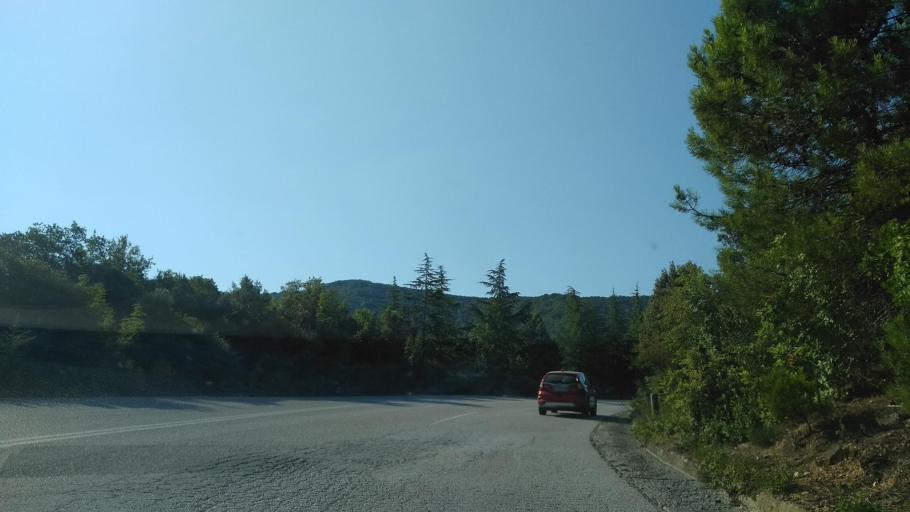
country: GR
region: Central Macedonia
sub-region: Nomos Chalkidikis
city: Stratonion
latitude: 40.5430
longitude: 23.8291
